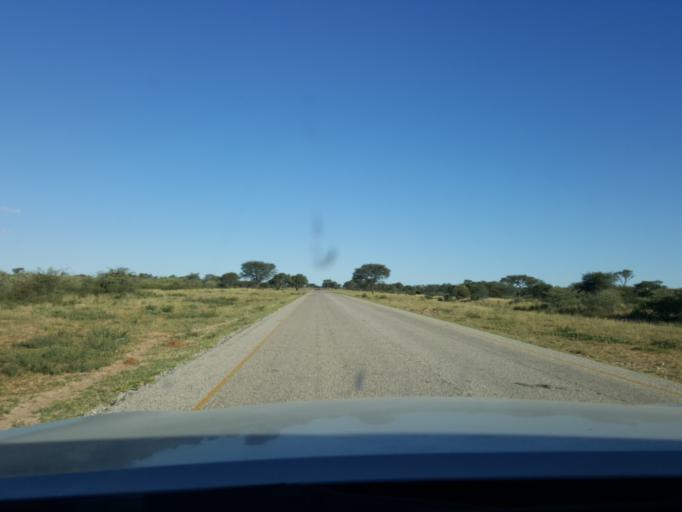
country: BW
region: Kgalagadi
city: Kang
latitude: -24.0153
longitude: 23.0320
